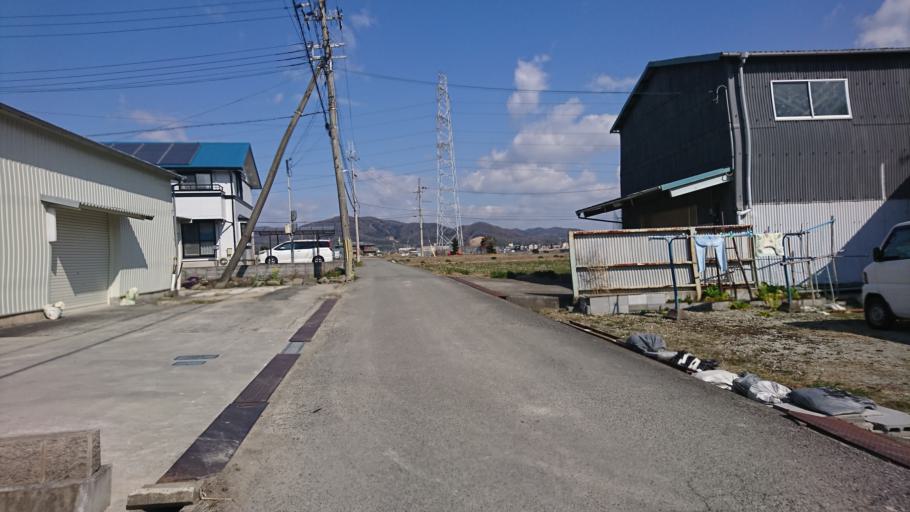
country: JP
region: Hyogo
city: Kakogawacho-honmachi
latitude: 34.8055
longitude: 134.8063
